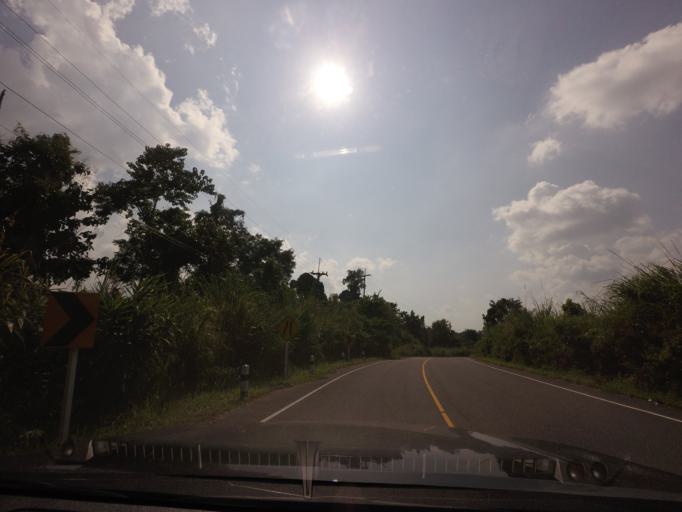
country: TH
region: Nan
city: Santi Suk
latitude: 18.9727
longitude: 101.0271
